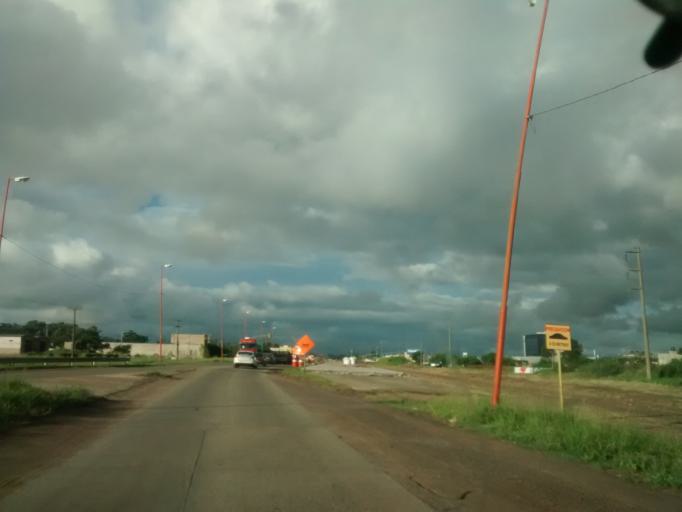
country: AR
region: Chaco
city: Fontana
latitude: -27.4493
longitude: -59.0270
